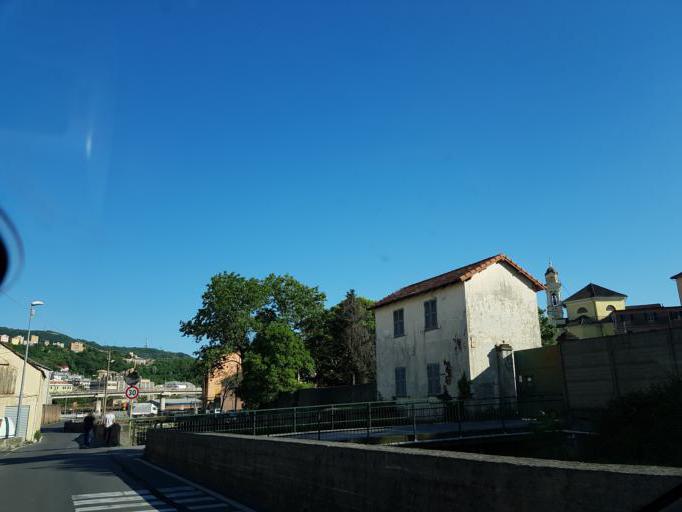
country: IT
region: Liguria
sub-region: Provincia di Genova
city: Genoa
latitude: 44.4531
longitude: 8.8907
